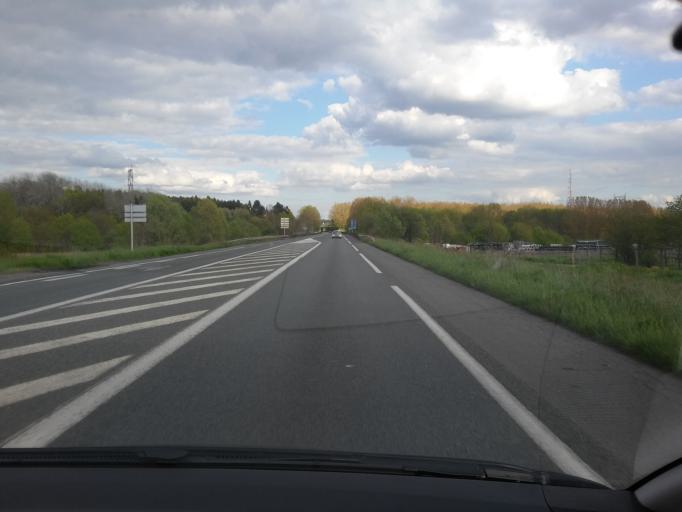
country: FR
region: Picardie
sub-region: Departement de l'Oise
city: Remy
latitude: 49.4023
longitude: 2.6910
